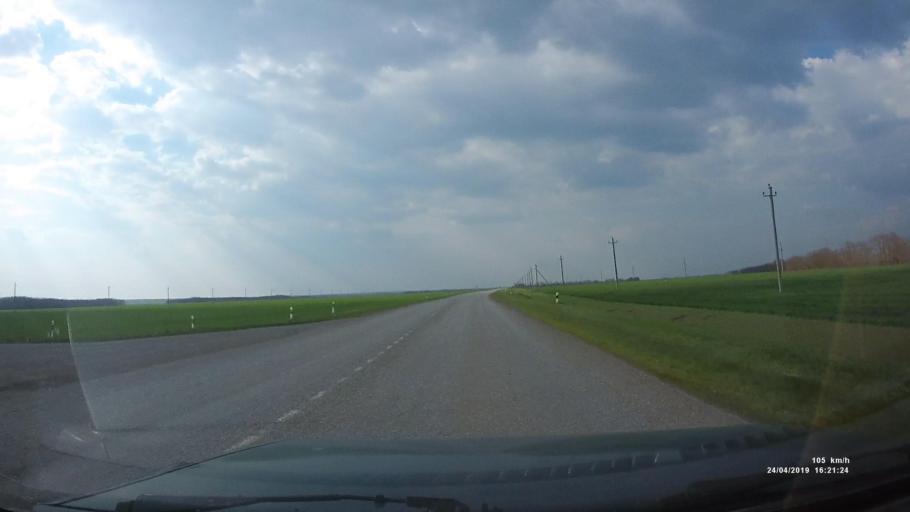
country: RU
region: Rostov
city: Orlovskiy
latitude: 46.8046
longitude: 42.0655
